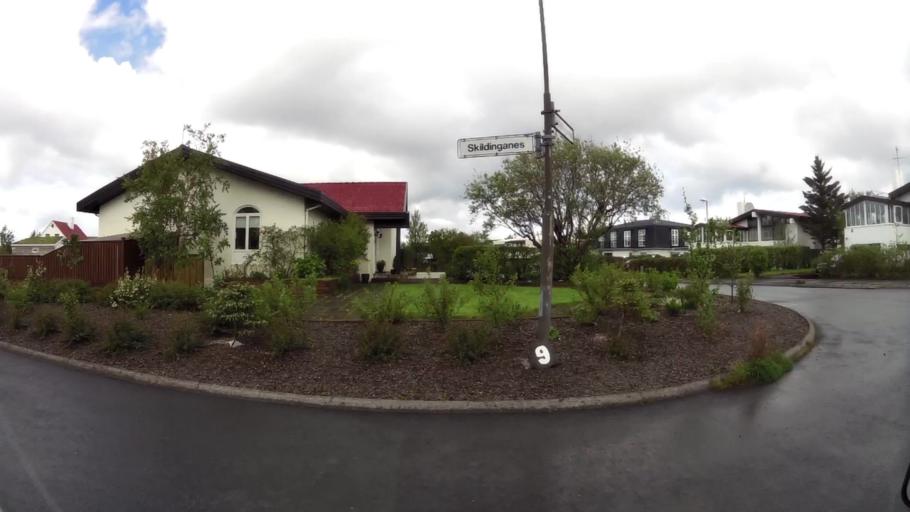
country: IS
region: Capital Region
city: Seltjarnarnes
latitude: 64.1299
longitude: -21.9562
